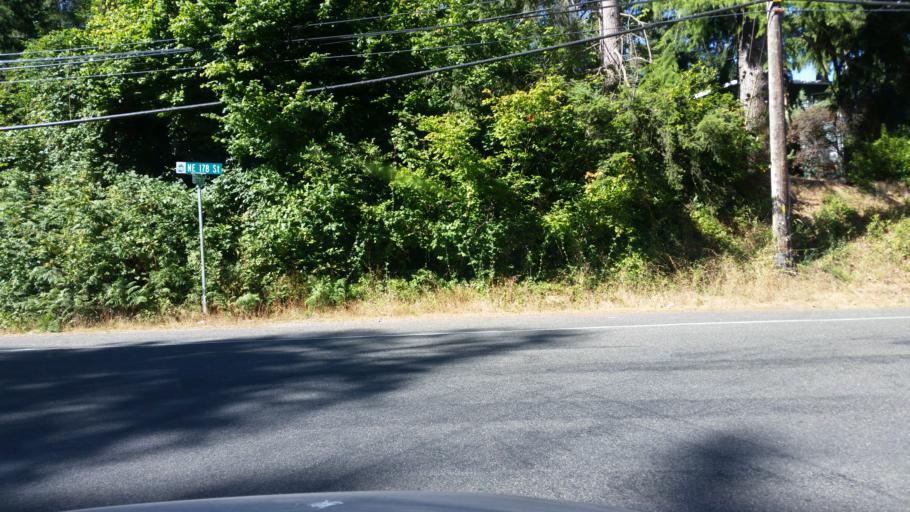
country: US
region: Washington
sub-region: King County
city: Lake Forest Park
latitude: 47.7584
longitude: -122.3042
